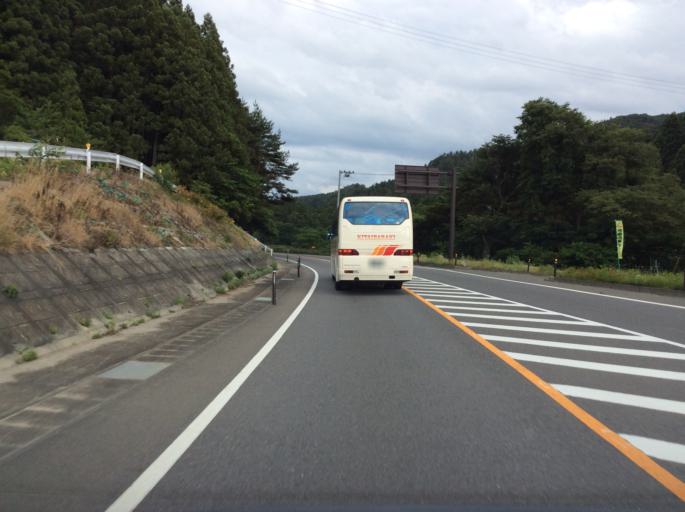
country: JP
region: Fukushima
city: Iwaki
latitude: 37.0827
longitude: 140.7813
